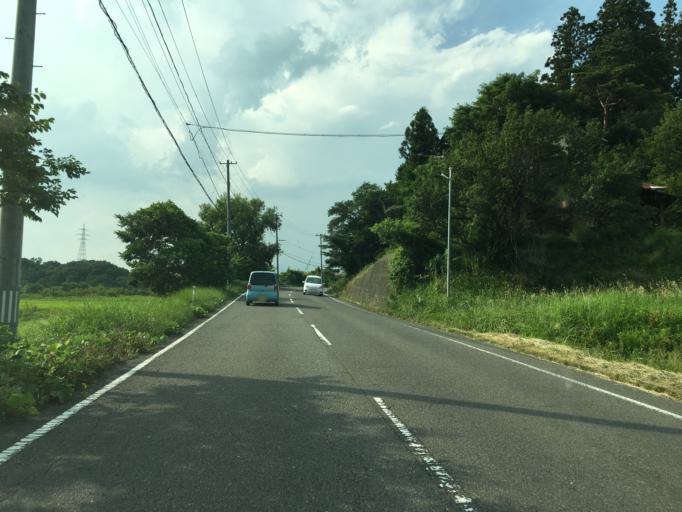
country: JP
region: Fukushima
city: Miharu
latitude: 37.4550
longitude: 140.4269
